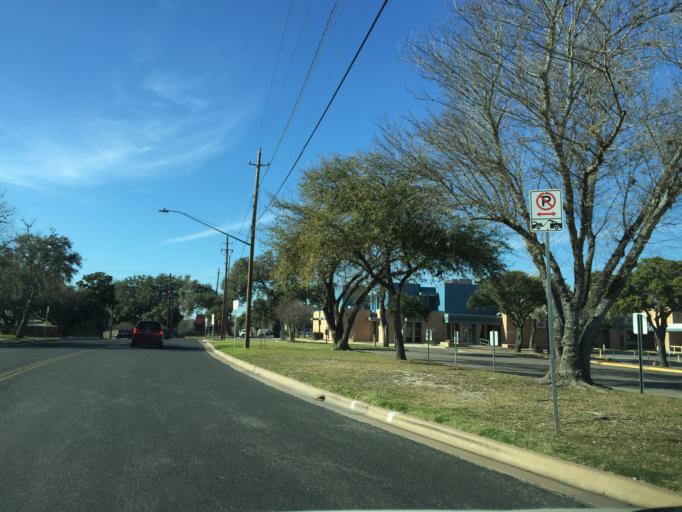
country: US
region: Texas
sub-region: Travis County
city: Austin
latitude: 30.2366
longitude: -97.7538
